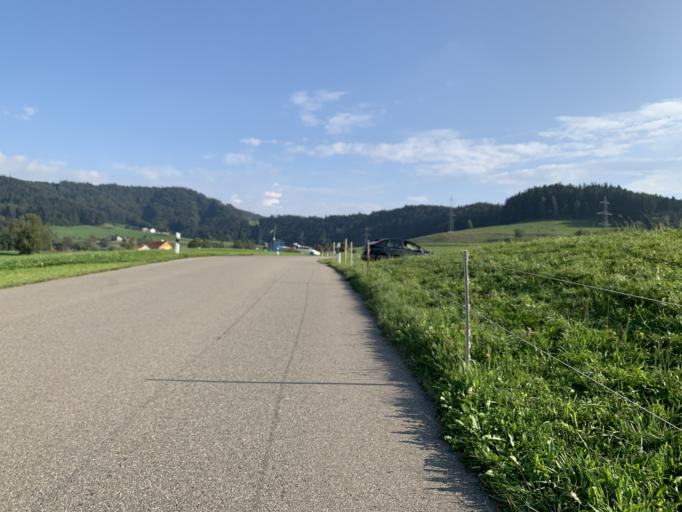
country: CH
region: Zurich
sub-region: Bezirk Hinwil
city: Baretswil
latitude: 47.3283
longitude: 8.8647
